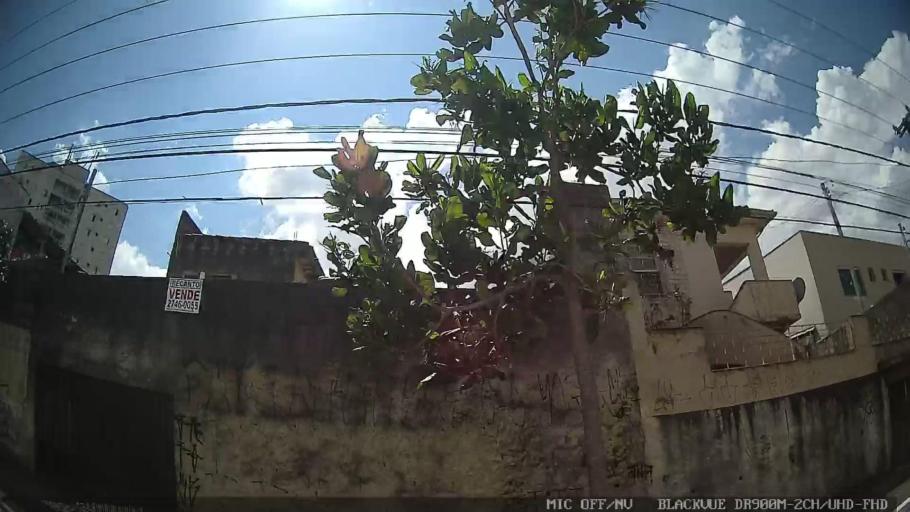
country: BR
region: Sao Paulo
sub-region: Ferraz De Vasconcelos
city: Ferraz de Vasconcelos
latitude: -23.5530
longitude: -46.4655
